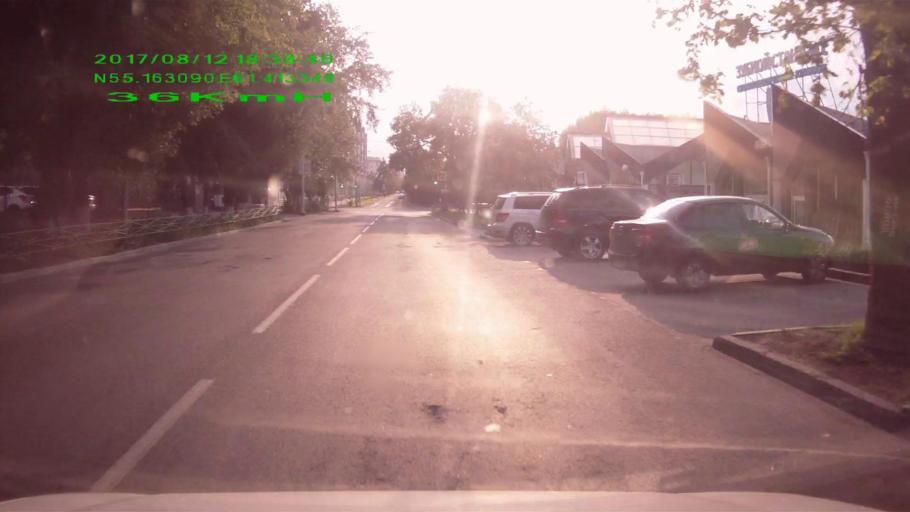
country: RU
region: Chelyabinsk
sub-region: Gorod Chelyabinsk
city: Chelyabinsk
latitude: 55.1627
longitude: 61.4066
